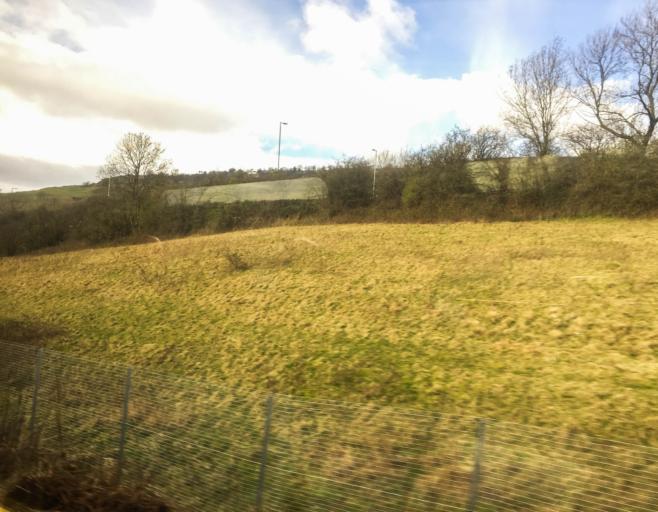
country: GB
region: Scotland
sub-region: West Dunbartonshire
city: Old Kilpatrick
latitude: 55.9278
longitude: -4.4621
